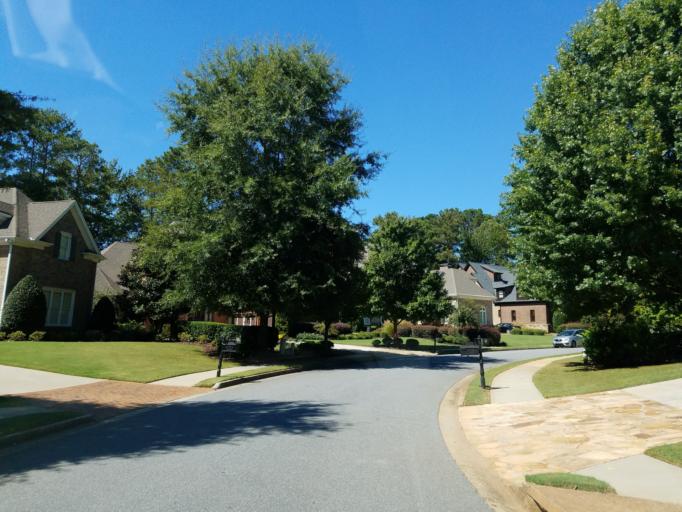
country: US
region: Georgia
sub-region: Cobb County
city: Marietta
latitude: 33.9750
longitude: -84.4637
